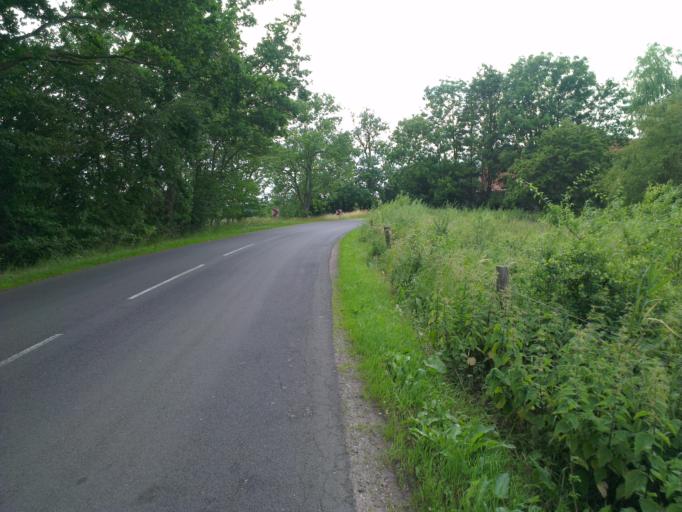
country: DK
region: Capital Region
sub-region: Frederikssund Kommune
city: Skibby
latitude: 55.7393
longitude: 11.9956
